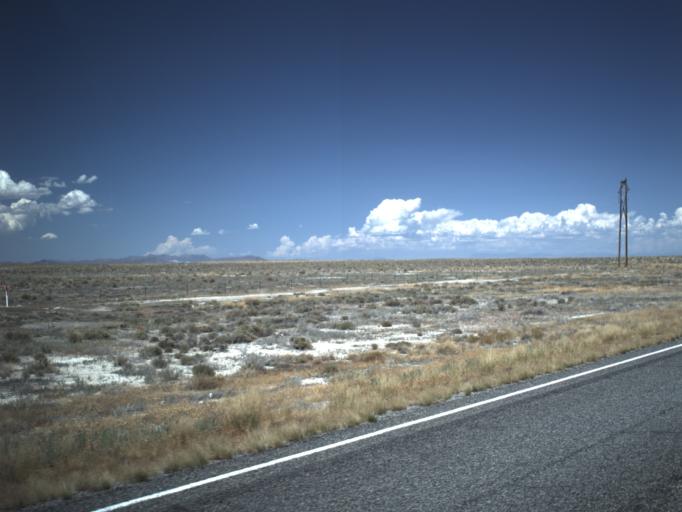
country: US
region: Utah
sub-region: Millard County
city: Delta
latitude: 39.1716
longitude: -113.0326
